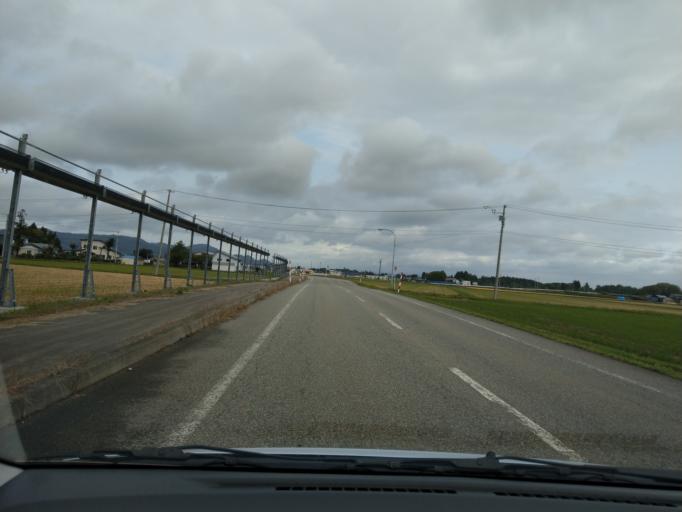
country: JP
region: Akita
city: Omagari
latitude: 39.3924
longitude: 140.4838
